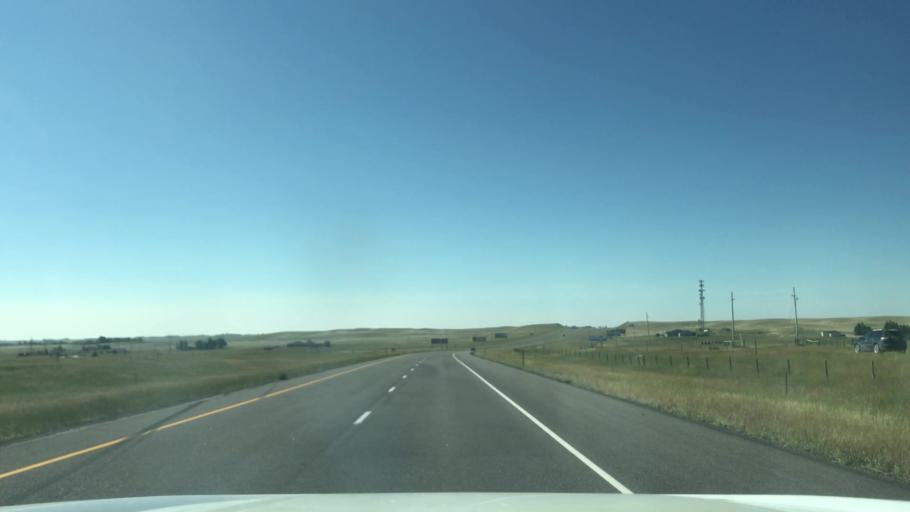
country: US
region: Wyoming
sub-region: Laramie County
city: Ranchettes
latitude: 41.2560
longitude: -104.8397
